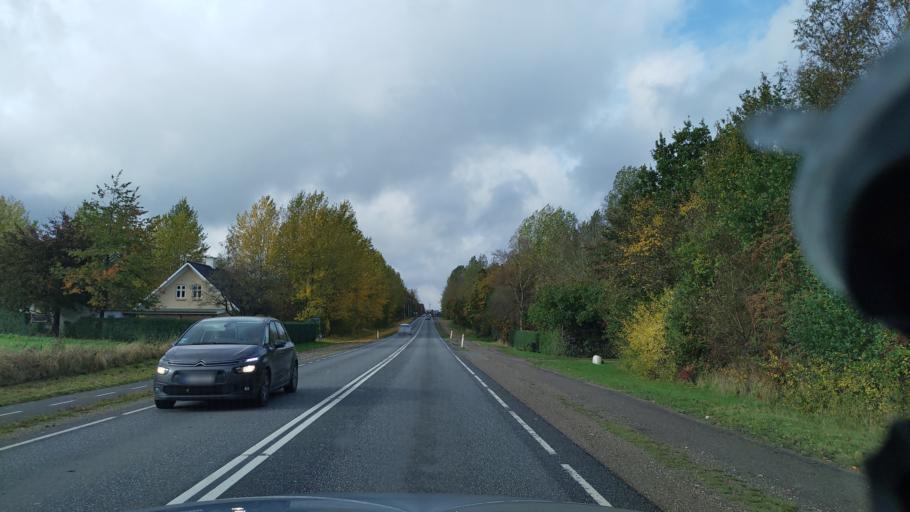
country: DK
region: Zealand
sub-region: Naestved Kommune
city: Fensmark
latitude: 55.2587
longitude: 11.8677
